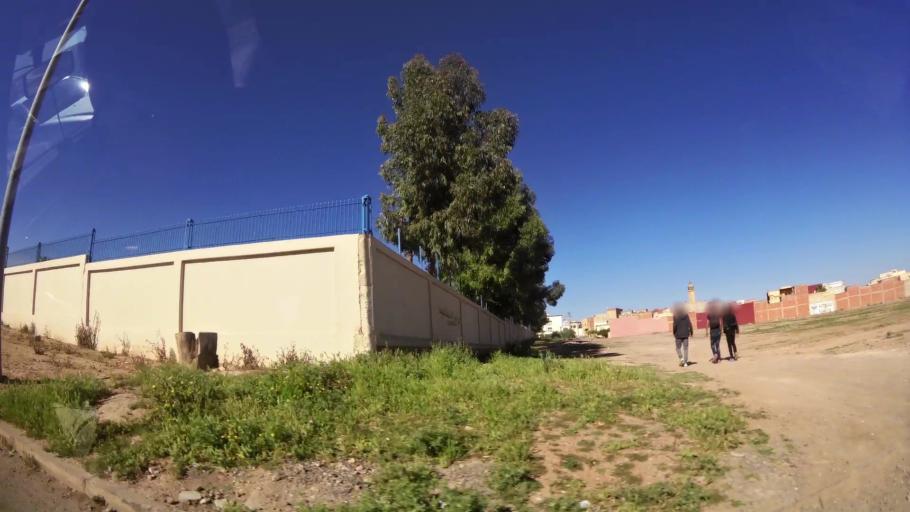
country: MA
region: Oriental
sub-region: Oujda-Angad
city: Oujda
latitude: 34.6548
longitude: -1.8888
